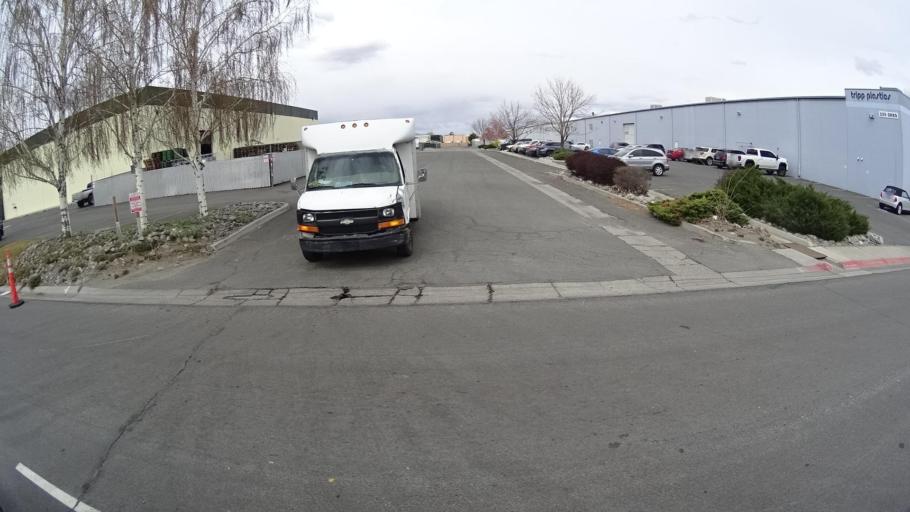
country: US
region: Nevada
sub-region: Washoe County
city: Sparks
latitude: 39.5217
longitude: -119.7463
